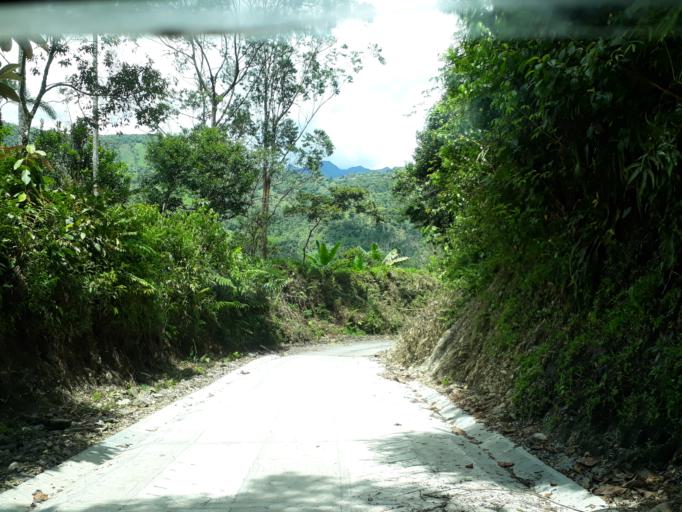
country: CO
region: Cundinamarca
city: Topaipi
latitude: 5.3519
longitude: -74.2002
